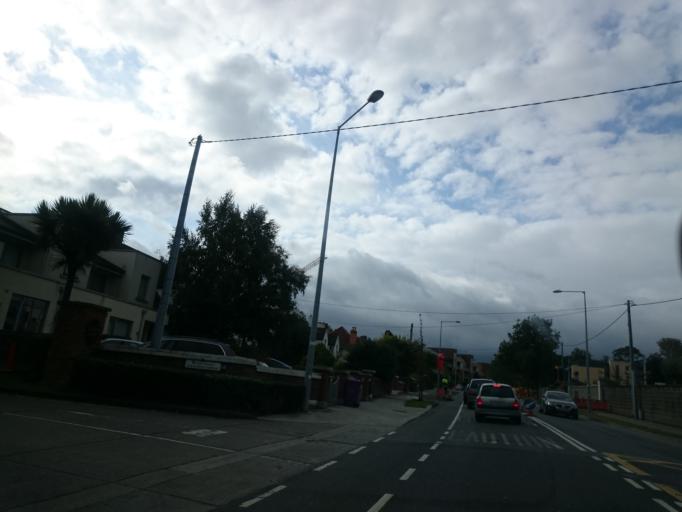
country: IE
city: Clonskeagh
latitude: 53.3013
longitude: -6.2334
